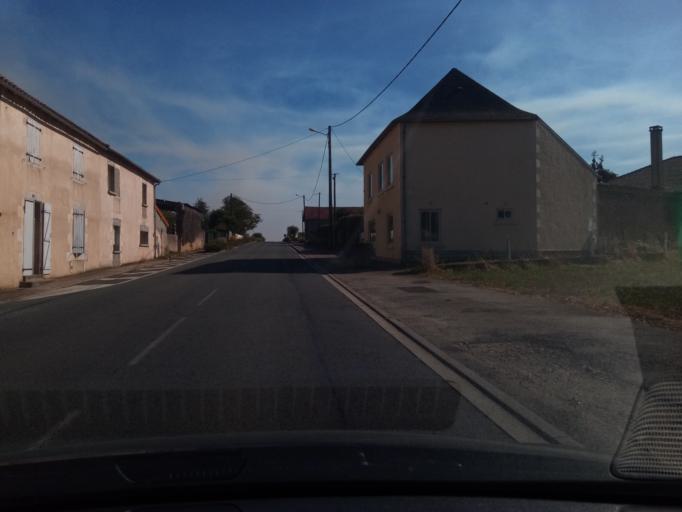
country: FR
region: Poitou-Charentes
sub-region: Departement de la Vienne
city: Saint-Savin
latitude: 46.5050
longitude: 0.7761
